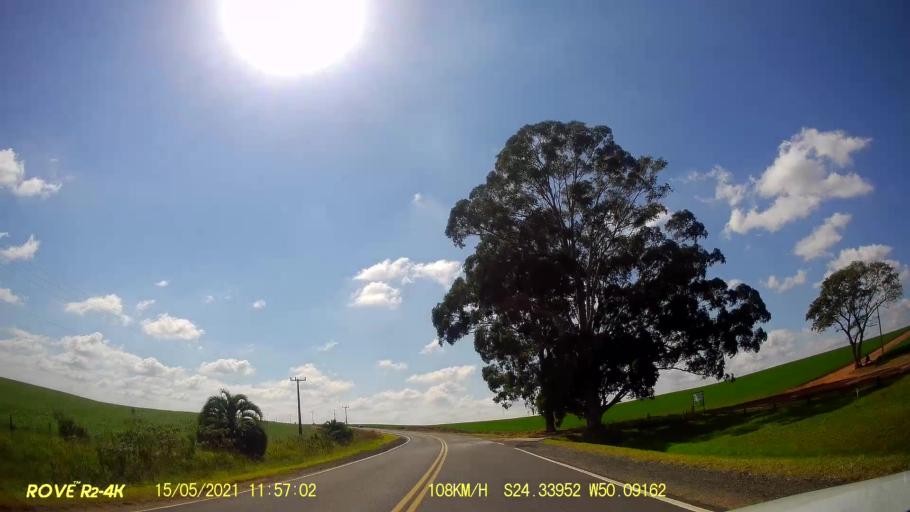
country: BR
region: Parana
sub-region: Pirai Do Sul
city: Pirai do Sul
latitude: -24.3397
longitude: -50.0917
